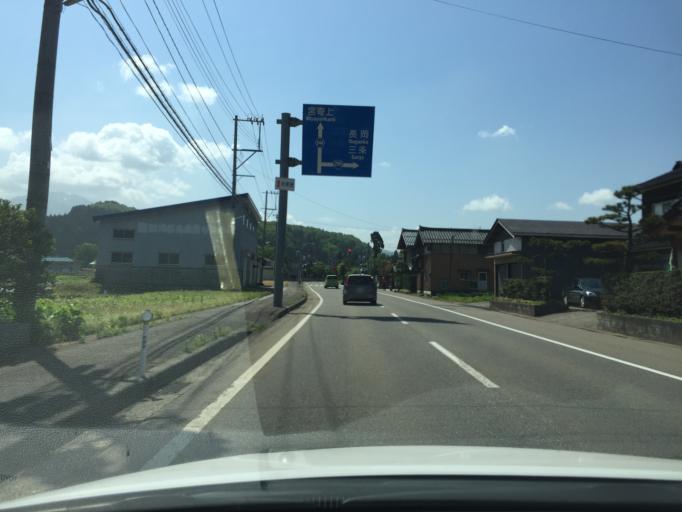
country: JP
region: Niigata
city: Kamo
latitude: 37.6098
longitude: 139.1049
